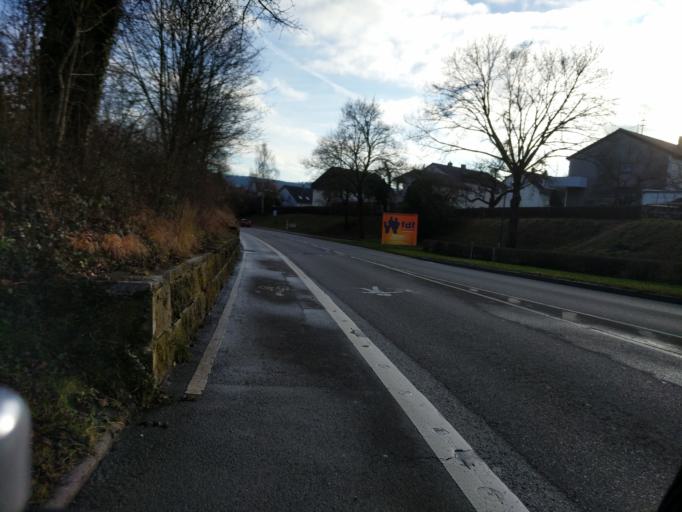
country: DE
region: Baden-Wuerttemberg
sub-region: Tuebingen Region
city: Rottenburg
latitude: 48.4841
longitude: 8.9358
